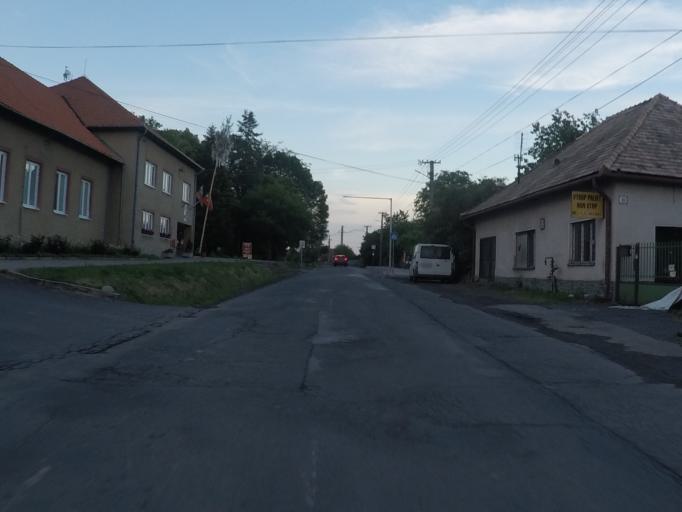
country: SK
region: Banskobystricky
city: Fil'akovo
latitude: 48.3076
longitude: 19.8008
